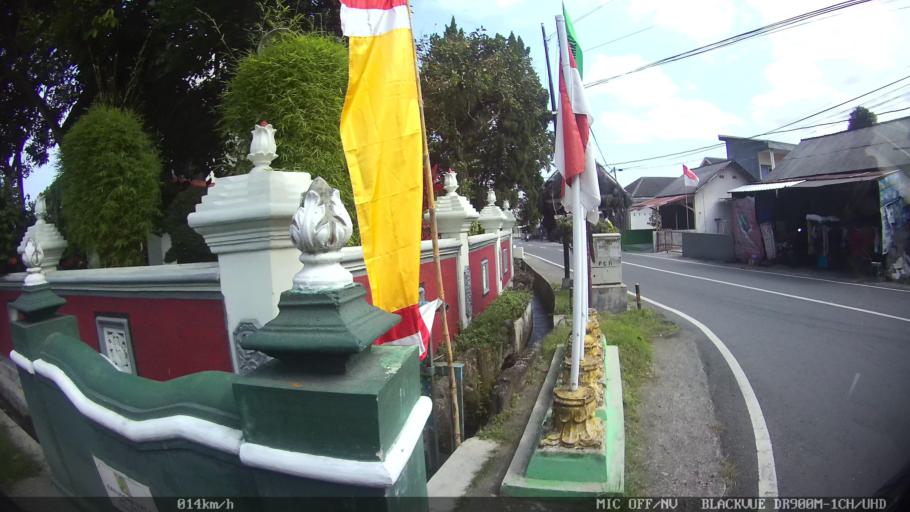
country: ID
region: Daerah Istimewa Yogyakarta
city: Depok
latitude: -7.7355
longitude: 110.4142
